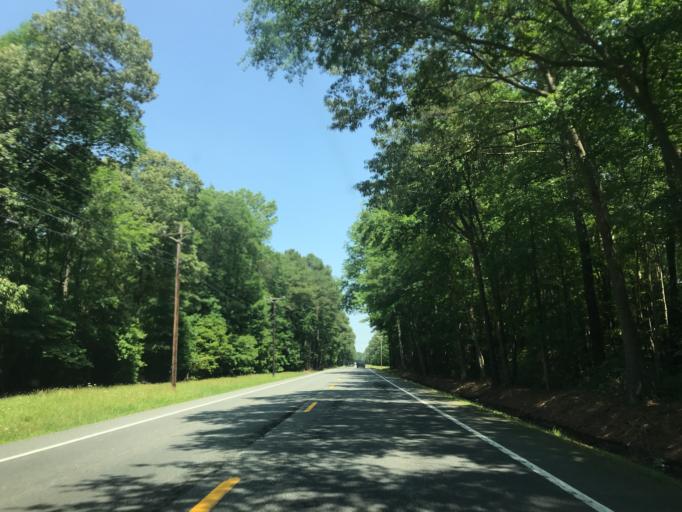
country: US
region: Maryland
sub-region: Dorchester County
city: Hurlock
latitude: 38.6326
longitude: -75.8004
